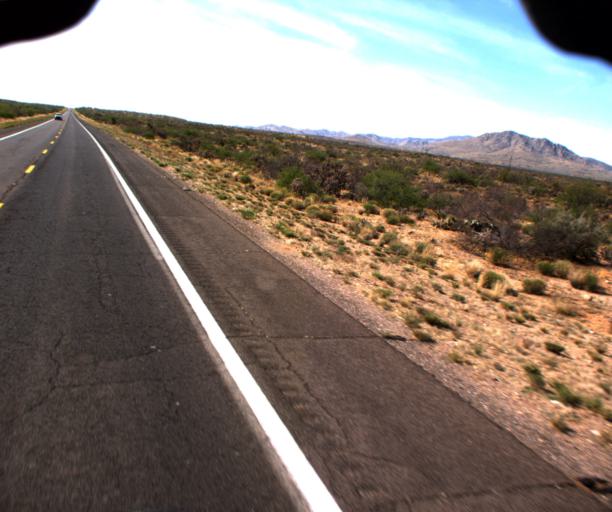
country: US
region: Arizona
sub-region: Graham County
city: Swift Trail Junction
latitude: 32.6447
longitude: -109.6964
